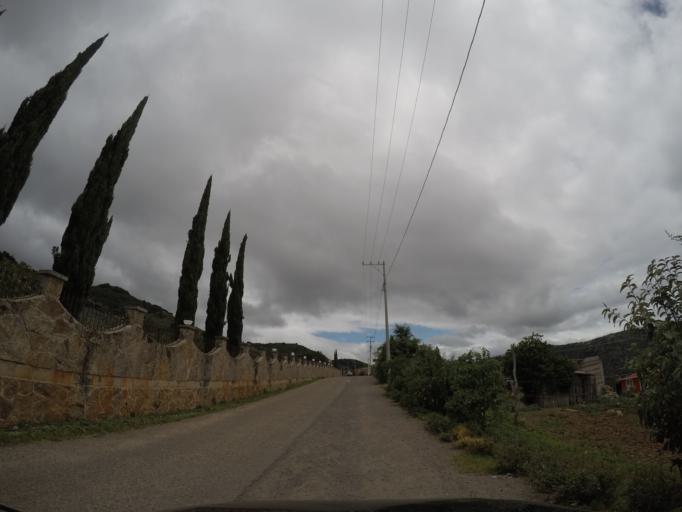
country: MX
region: Oaxaca
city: San Lorenzo Albarradas
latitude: 16.9000
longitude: -96.2609
